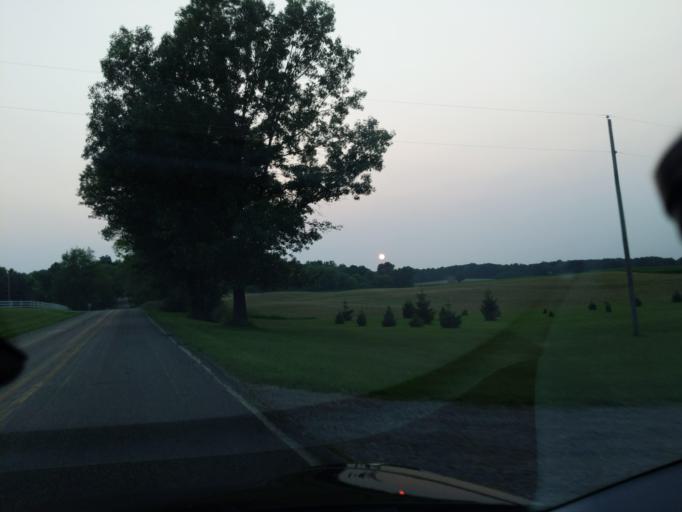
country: US
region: Michigan
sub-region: Ingham County
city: Leslie
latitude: 42.3495
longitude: -84.4756
